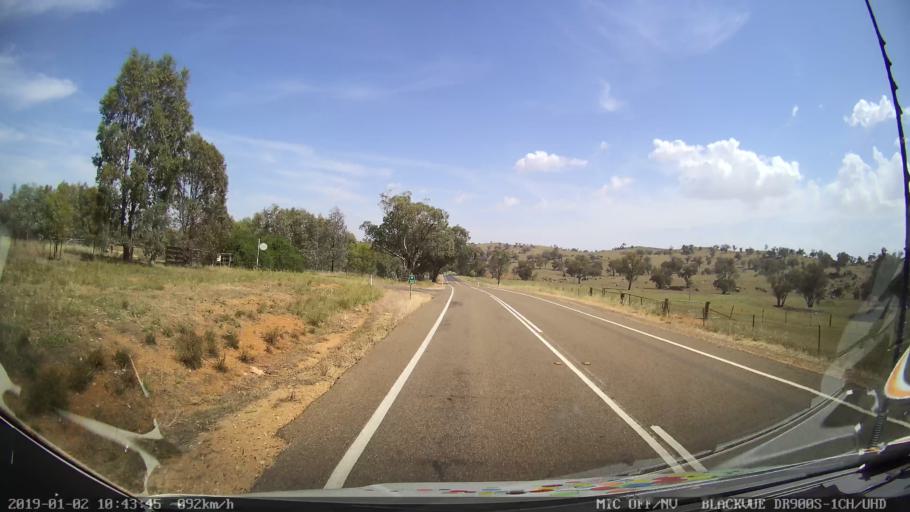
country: AU
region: New South Wales
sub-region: Cootamundra
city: Cootamundra
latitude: -34.7685
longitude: 148.3018
